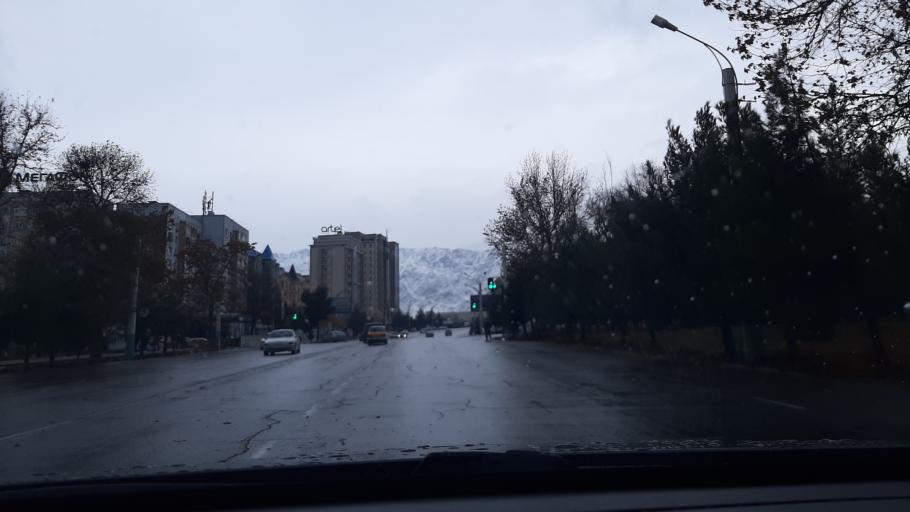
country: TJ
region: Viloyati Sughd
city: Khujand
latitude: 40.2970
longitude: 69.6161
